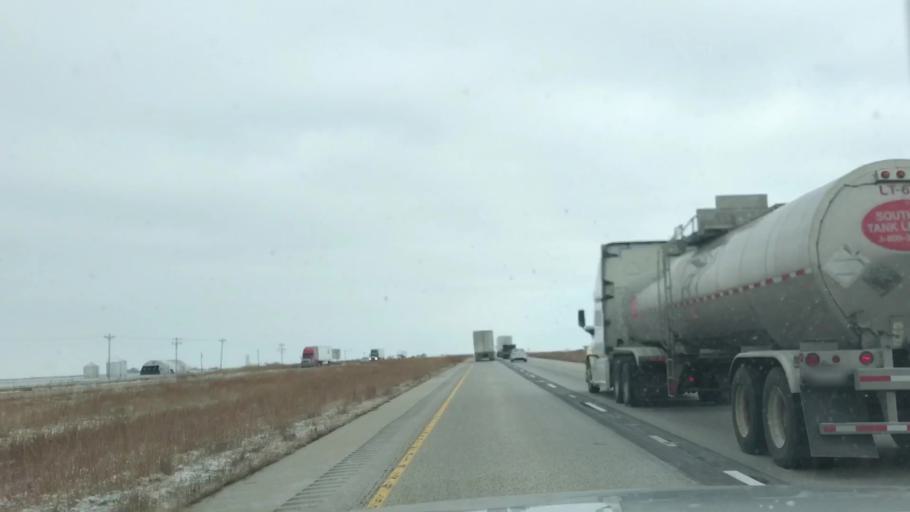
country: US
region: Illinois
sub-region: Sangamon County
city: Divernon
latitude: 39.4624
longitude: -89.6443
